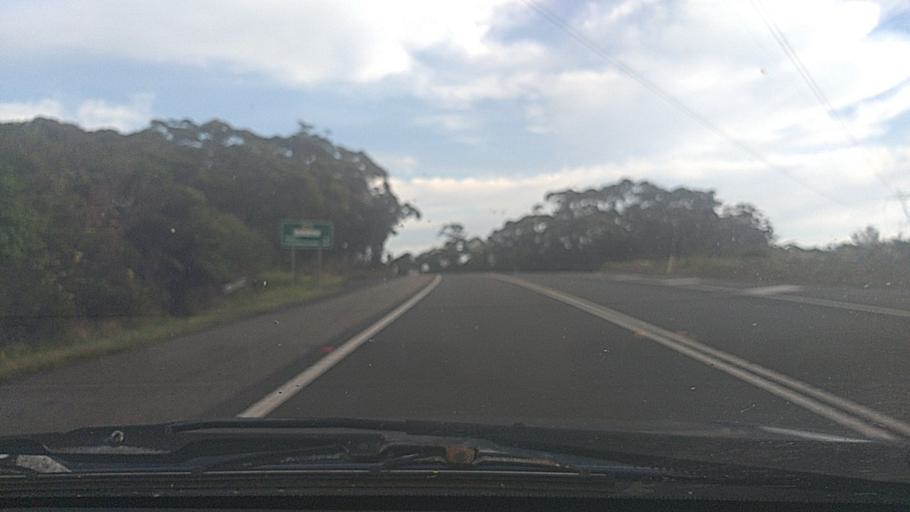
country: AU
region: New South Wales
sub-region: Wollongong
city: Bulli
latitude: -34.2990
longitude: 150.9056
